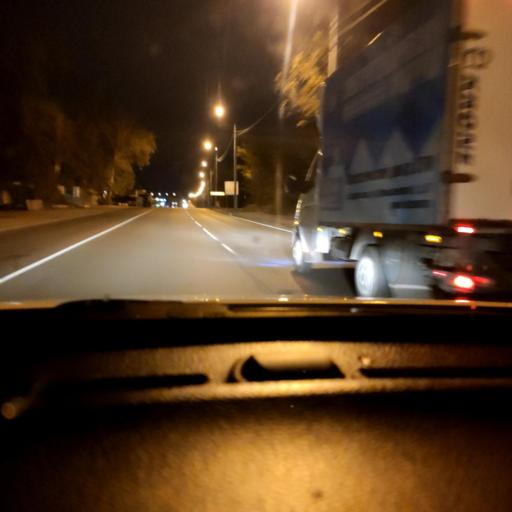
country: RU
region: Voronezj
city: Voronezh
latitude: 51.6703
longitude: 39.2717
